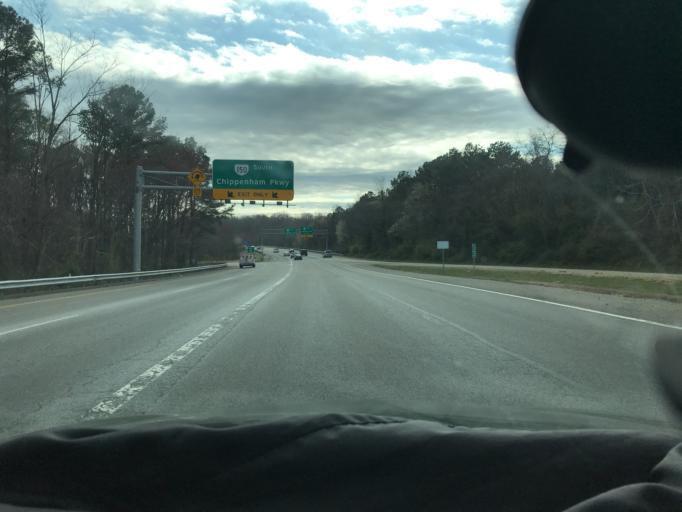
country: US
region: Virginia
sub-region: Chesterfield County
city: Bon Air
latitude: 37.5259
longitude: -77.5292
